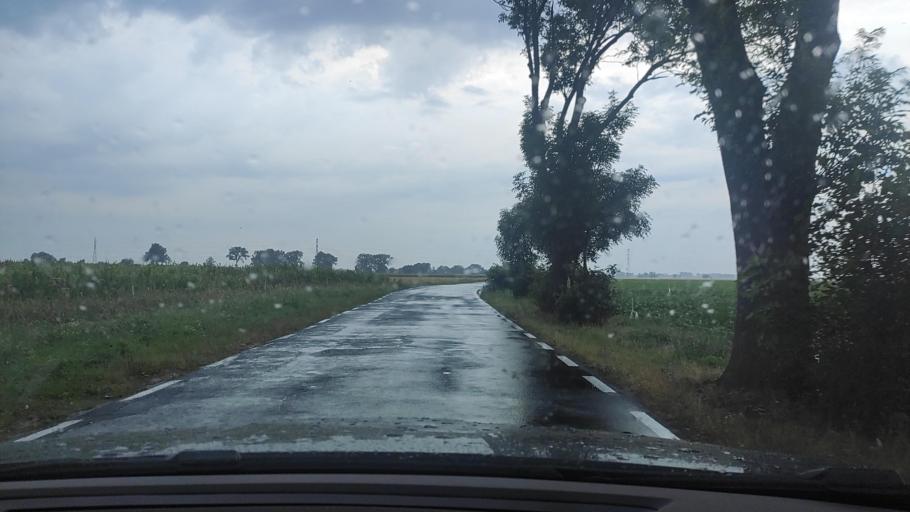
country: PL
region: Greater Poland Voivodeship
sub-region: Powiat poznanski
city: Kleszczewo
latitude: 52.2911
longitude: 17.1771
